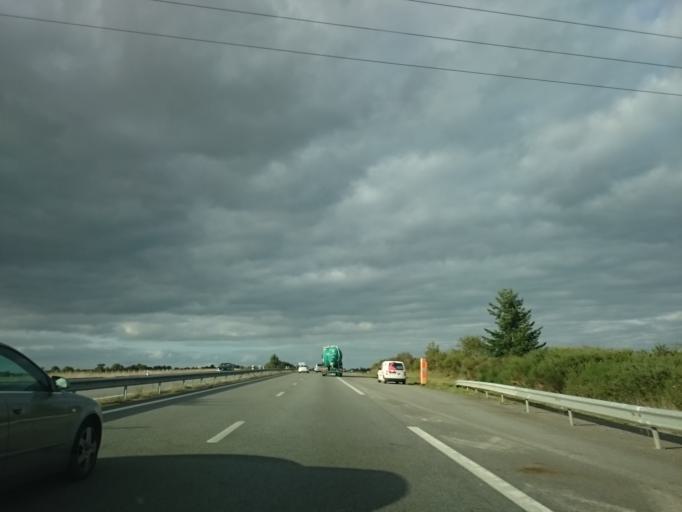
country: FR
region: Brittany
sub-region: Departement d'Ille-et-Vilaine
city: La Dominelais
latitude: 47.7666
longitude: -1.7100
